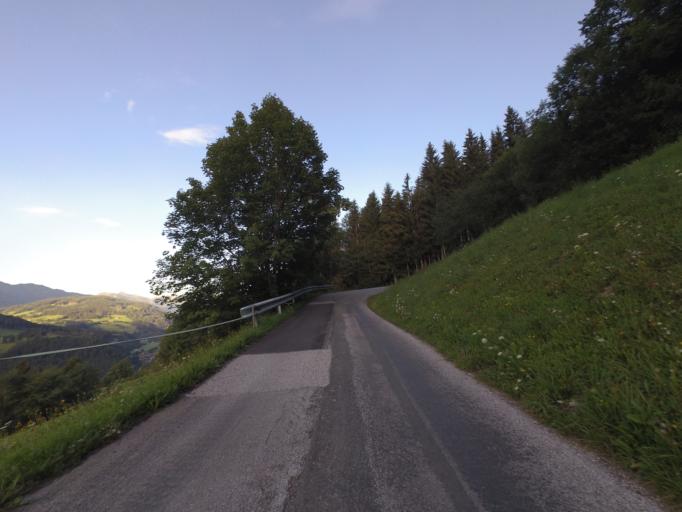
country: AT
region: Salzburg
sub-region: Politischer Bezirk Sankt Johann im Pongau
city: Goldegg
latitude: 47.3380
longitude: 13.1033
